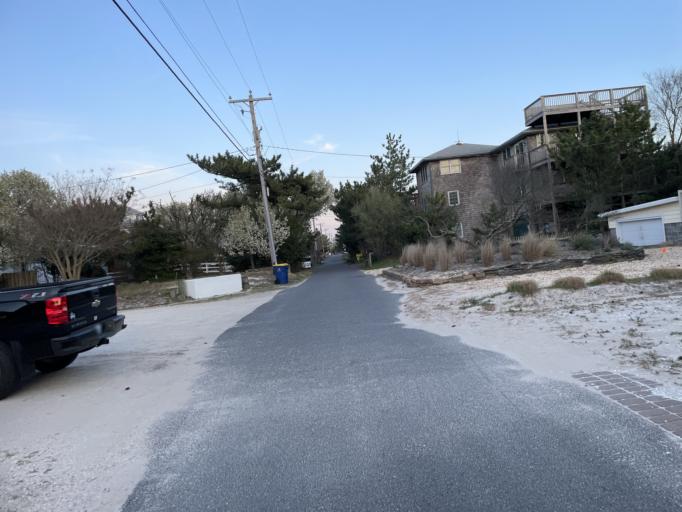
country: US
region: Delaware
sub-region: Sussex County
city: Lewes
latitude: 38.7848
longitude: -75.1476
